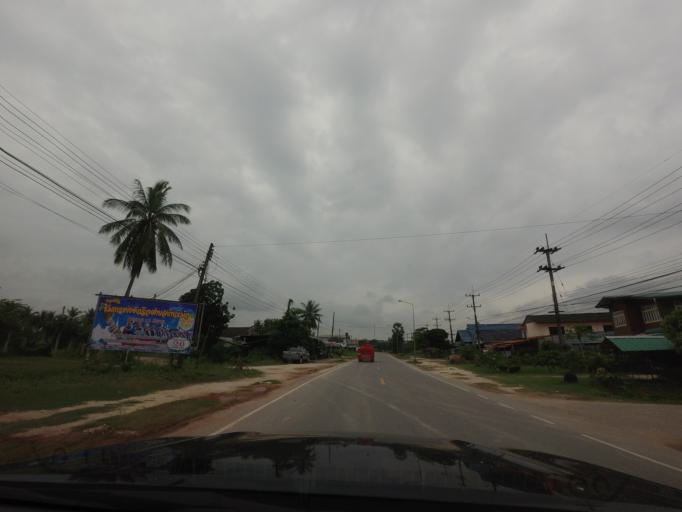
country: TH
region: Nong Khai
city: Si Chiang Mai
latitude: 17.9610
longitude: 102.5247
